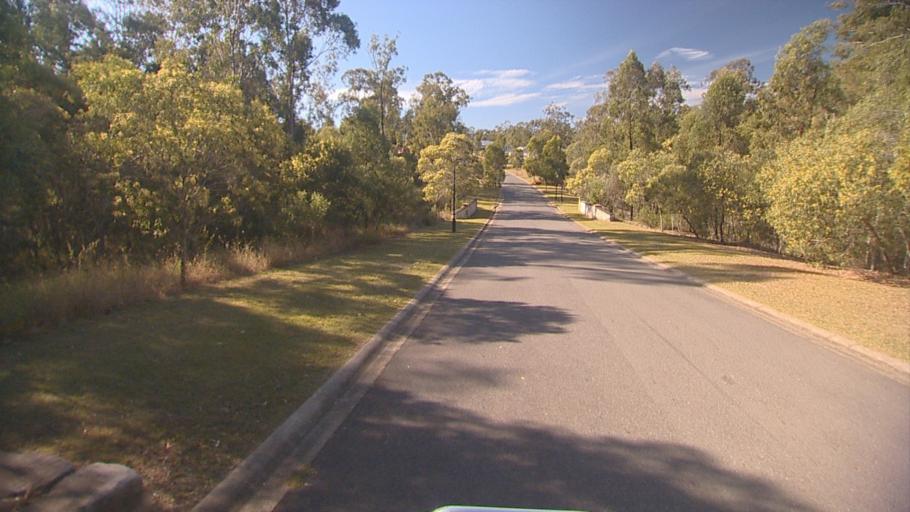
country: AU
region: Queensland
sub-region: Ipswich
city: Springfield Lakes
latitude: -27.7255
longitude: 152.9234
